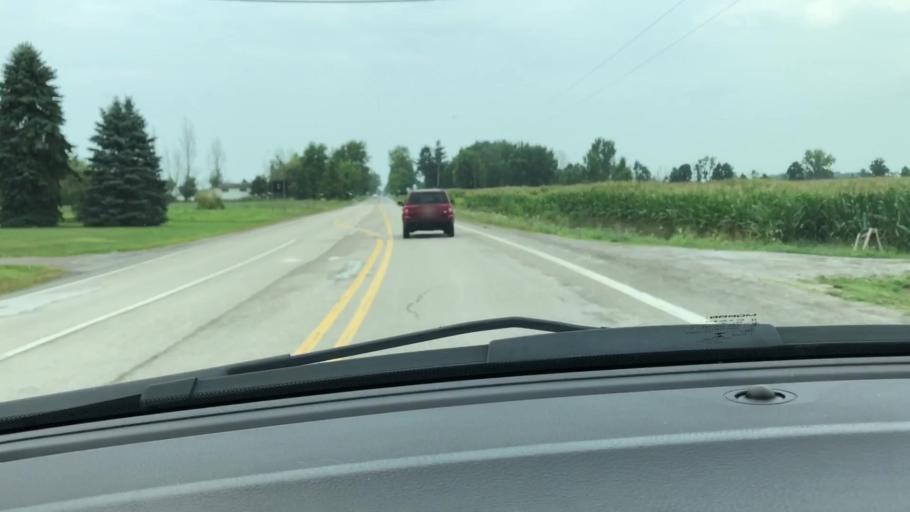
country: US
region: Michigan
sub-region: Saginaw County
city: Freeland
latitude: 43.5426
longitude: -84.0903
